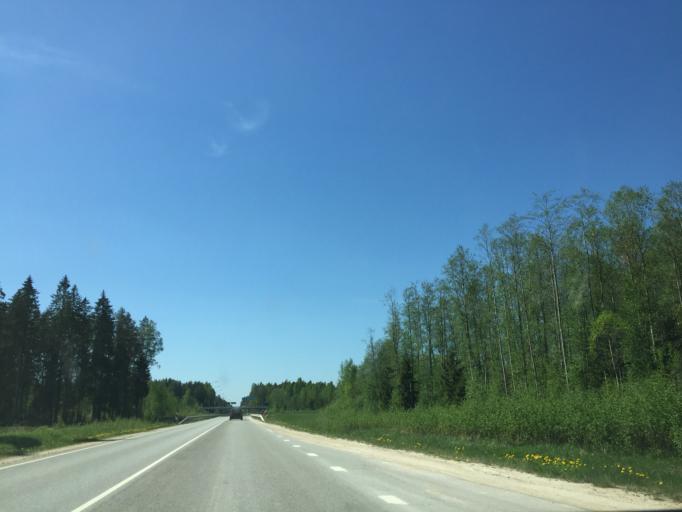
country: LV
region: Ogre
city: Ogre
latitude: 56.8477
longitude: 24.6809
